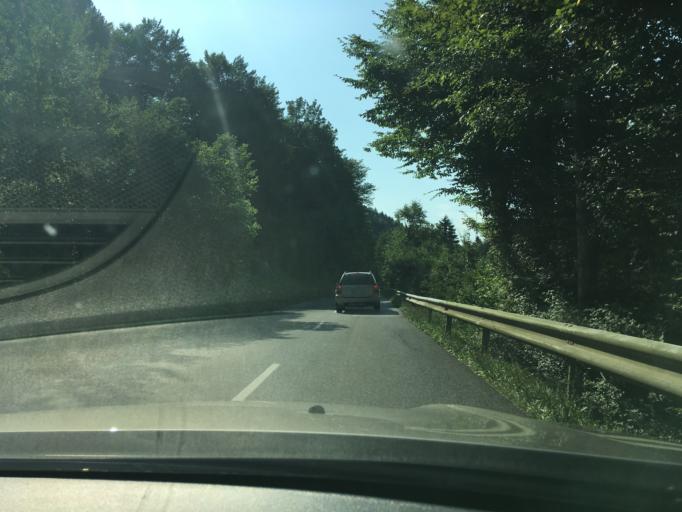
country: SI
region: Dolenjske Toplice
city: Dolenjske Toplice
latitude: 45.7658
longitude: 15.0543
